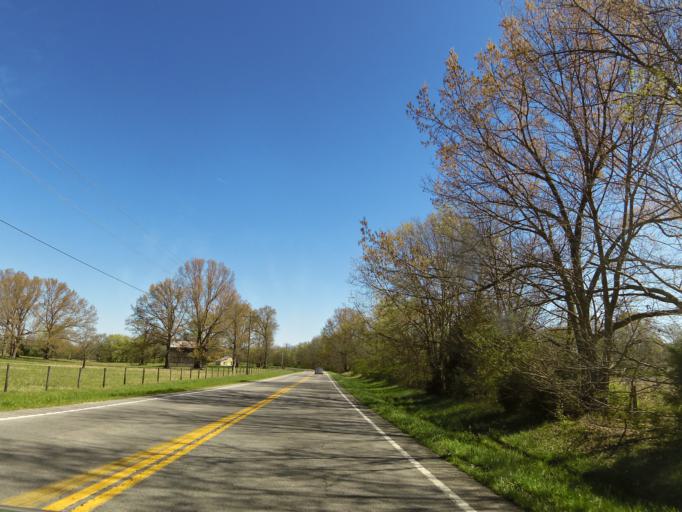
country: US
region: Tennessee
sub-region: Robertson County
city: Springfield
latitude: 36.5717
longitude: -86.8591
